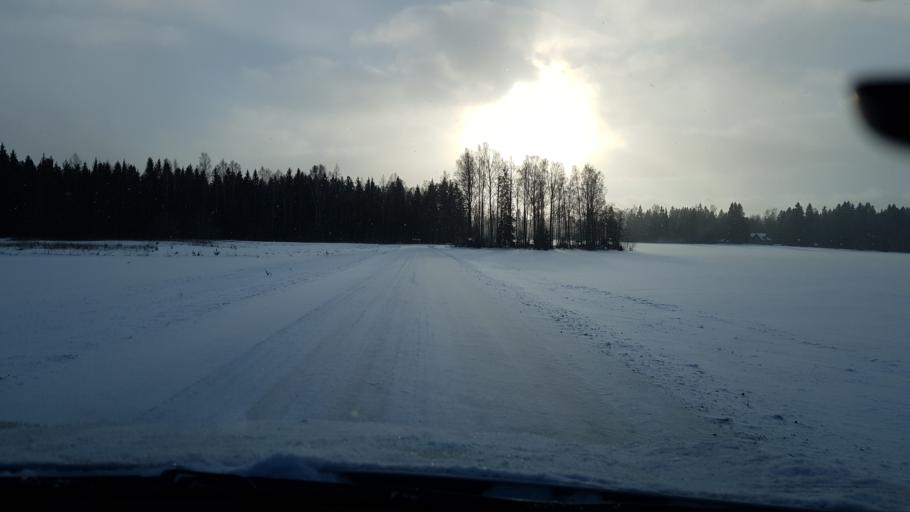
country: EE
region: Harju
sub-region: Nissi vald
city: Turba
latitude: 59.1999
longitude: 24.1397
